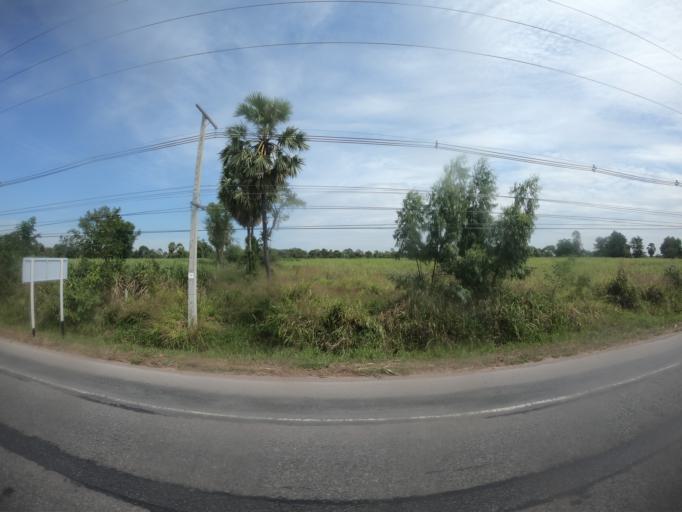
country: TH
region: Maha Sarakham
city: Chiang Yuen
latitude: 16.4262
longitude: 103.0670
